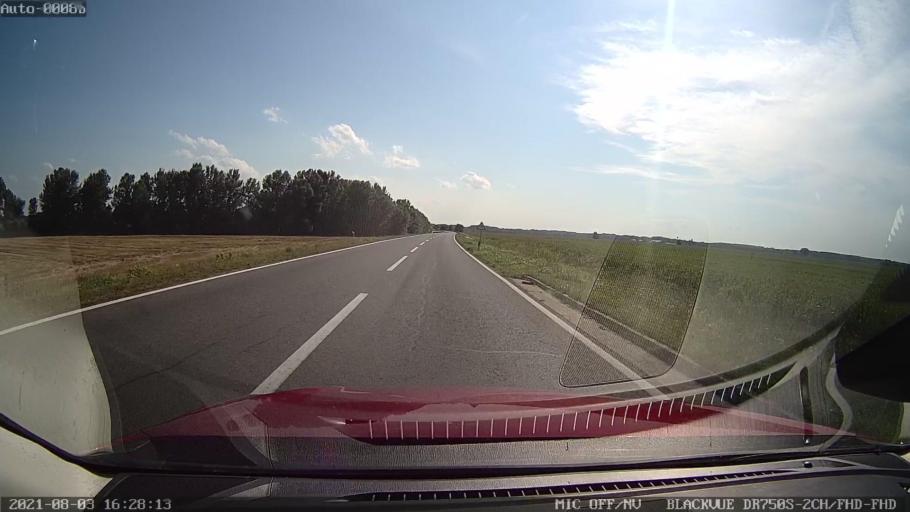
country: HR
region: Osjecko-Baranjska
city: Darda
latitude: 45.6113
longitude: 18.6698
